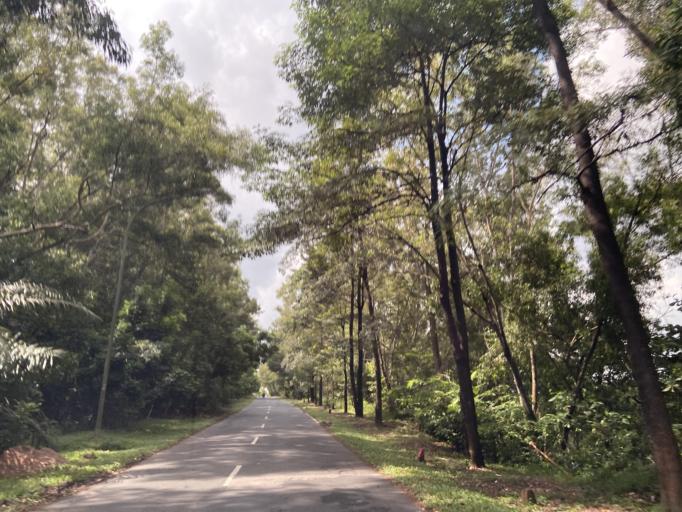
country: SG
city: Singapore
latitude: 1.1129
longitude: 104.0257
